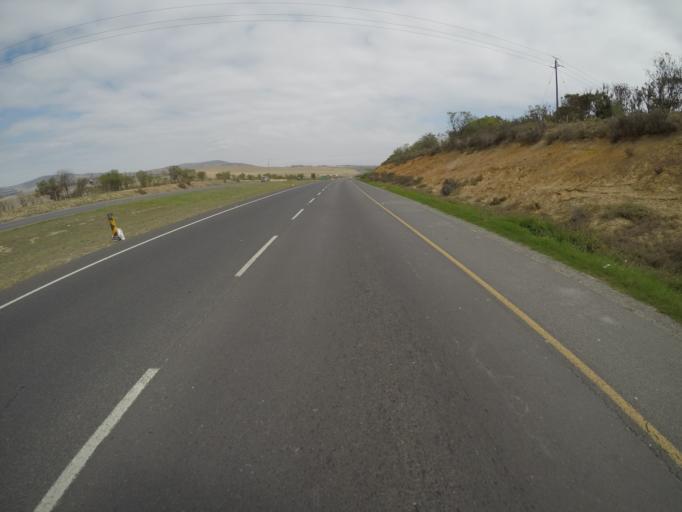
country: ZA
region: Western Cape
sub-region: City of Cape Town
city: Sunset Beach
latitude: -33.7849
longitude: 18.5490
